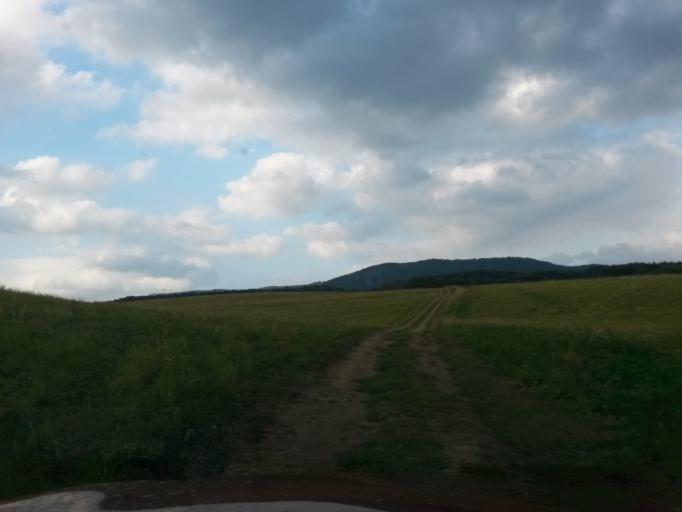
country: SK
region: Kosicky
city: Secovce
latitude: 48.8066
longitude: 21.4734
